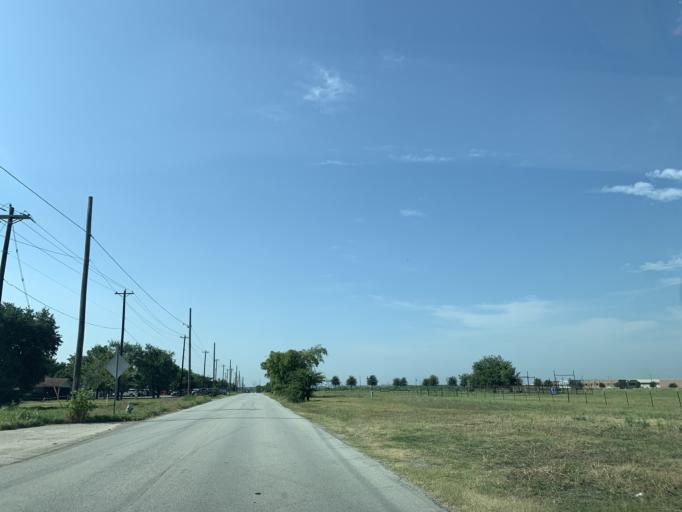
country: US
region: Texas
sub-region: Tarrant County
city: Blue Mound
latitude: 32.8950
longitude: -97.3070
